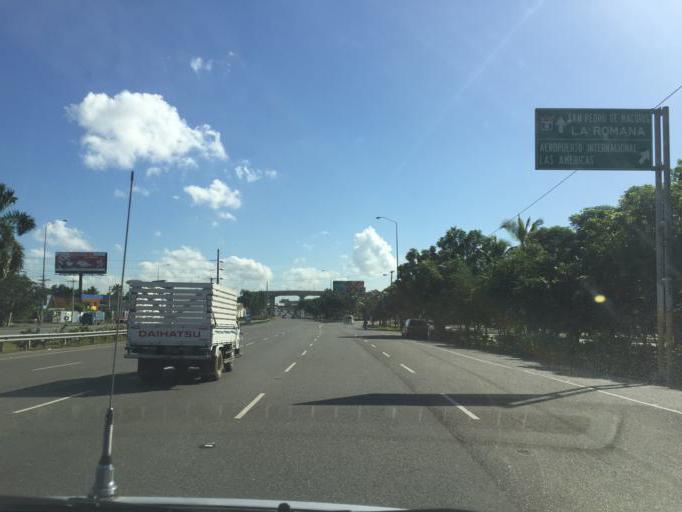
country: DO
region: Santo Domingo
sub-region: Santo Domingo
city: Boca Chica
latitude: 18.4506
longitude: -69.6848
